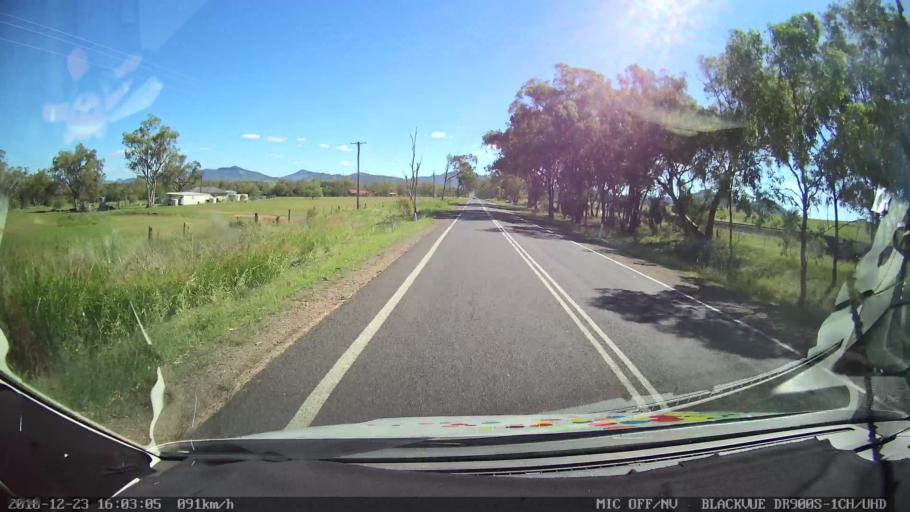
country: AU
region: New South Wales
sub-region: Tamworth Municipality
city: Phillip
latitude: -31.2395
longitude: 150.8037
